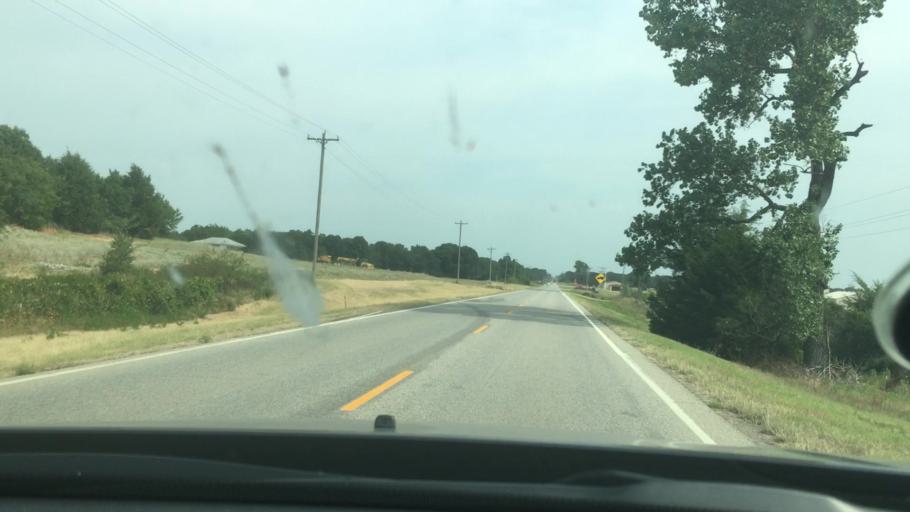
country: US
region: Oklahoma
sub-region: Bryan County
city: Durant
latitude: 34.2100
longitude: -96.4250
